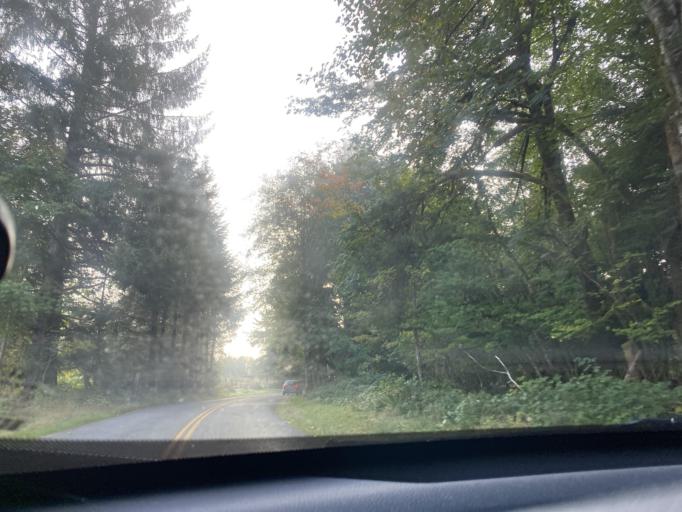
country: US
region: Washington
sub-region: Clallam County
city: Forks
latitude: 47.8174
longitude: -124.0388
